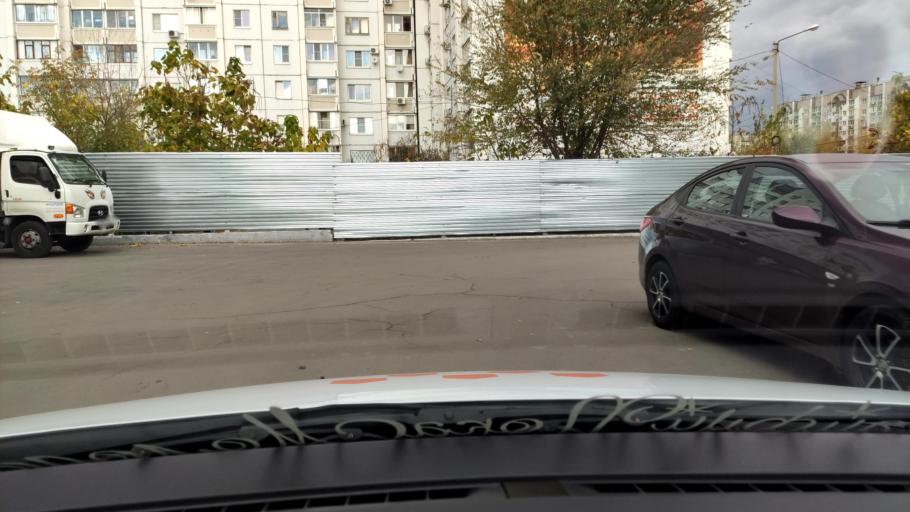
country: RU
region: Voronezj
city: Podgornoye
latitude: 51.7131
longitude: 39.1607
